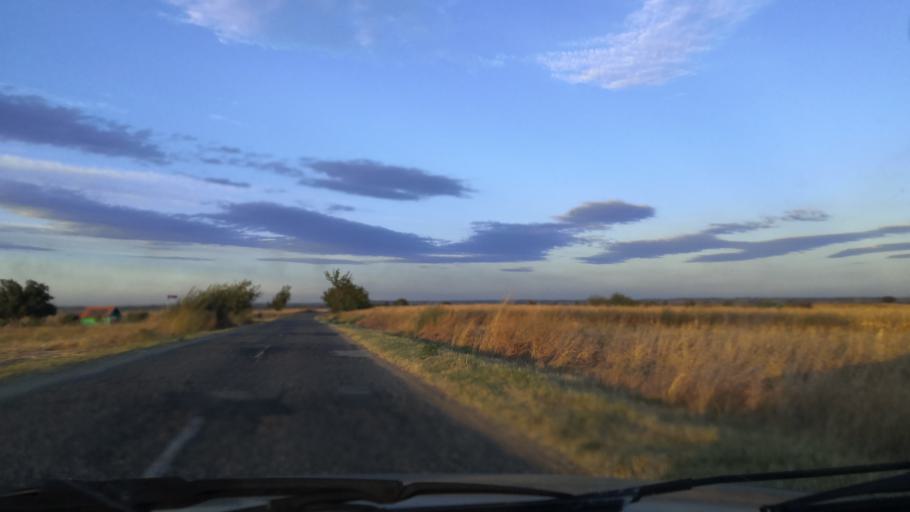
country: RO
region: Mehedinti
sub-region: Comuna Gruia
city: Izvoarele
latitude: 44.2581
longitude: 22.6341
